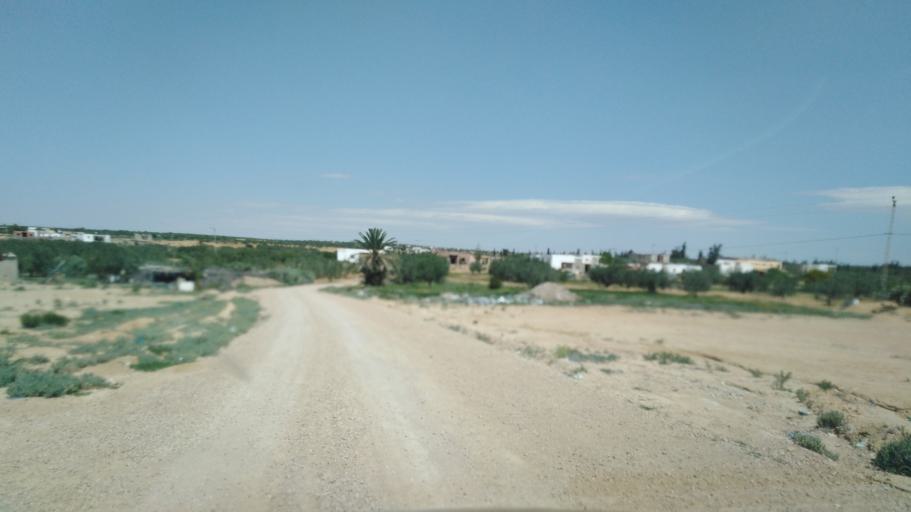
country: TN
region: Safaqis
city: Sfax
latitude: 34.7607
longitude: 10.5248
